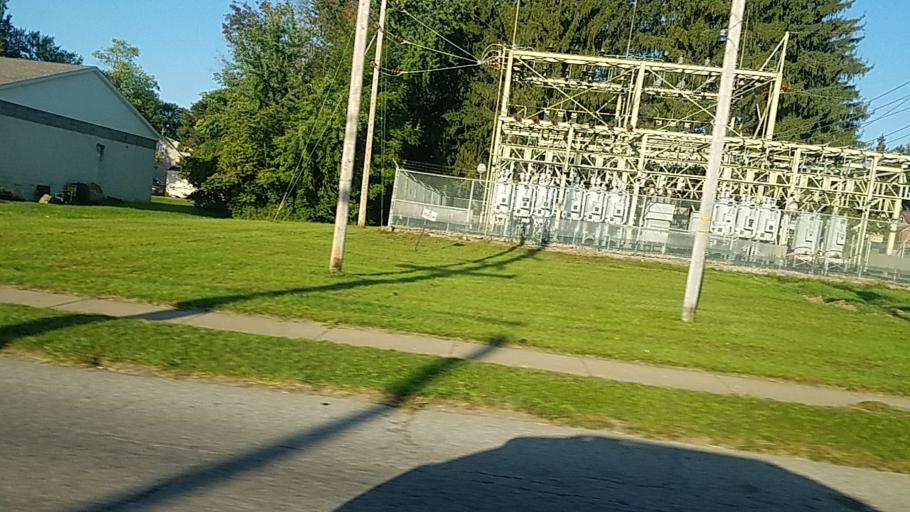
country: US
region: Ohio
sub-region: Mahoning County
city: Boardman
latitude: 41.0501
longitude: -80.6579
